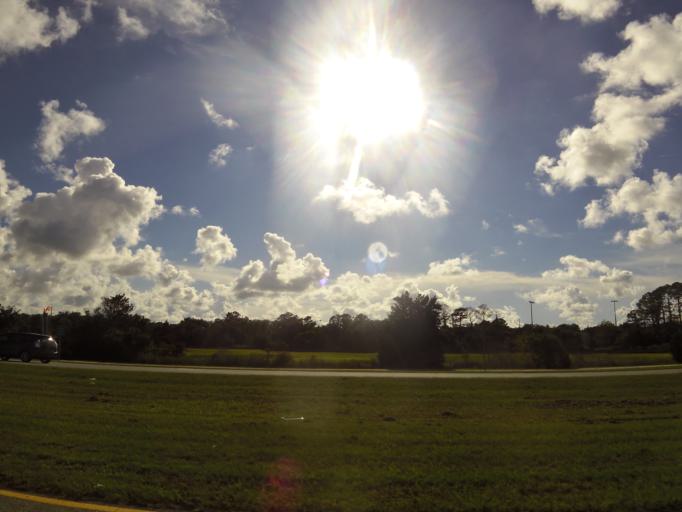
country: US
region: Georgia
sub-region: Glynn County
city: Brunswick
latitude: 31.1364
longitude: -81.4787
